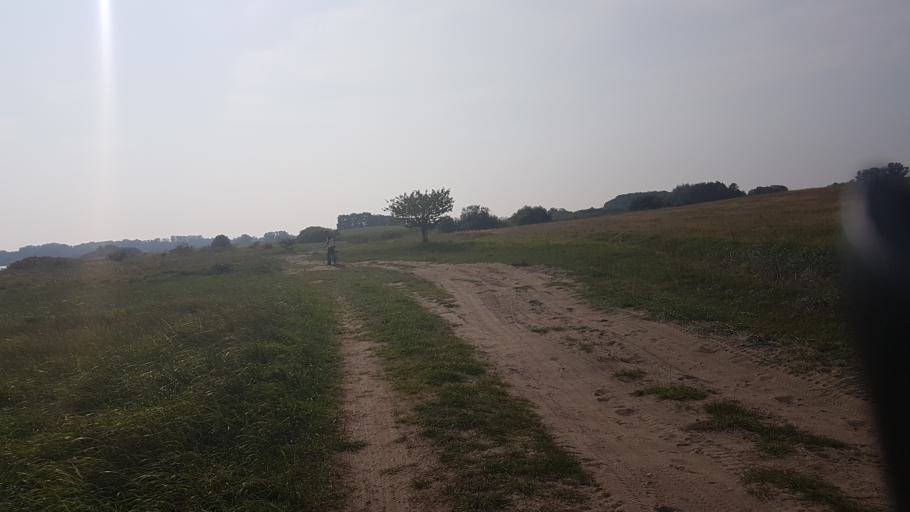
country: DE
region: Mecklenburg-Vorpommern
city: Garz
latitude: 54.3038
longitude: 13.4209
